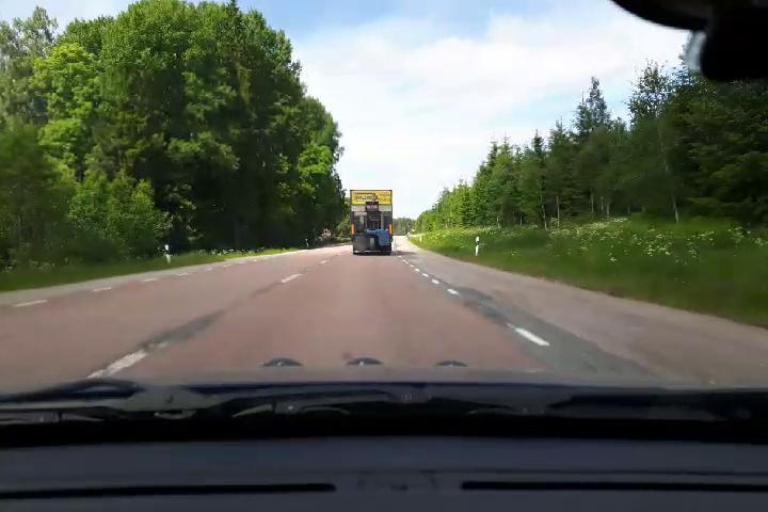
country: SE
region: Uppsala
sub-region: Osthammars Kommun
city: Bjorklinge
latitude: 60.1505
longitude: 17.4935
